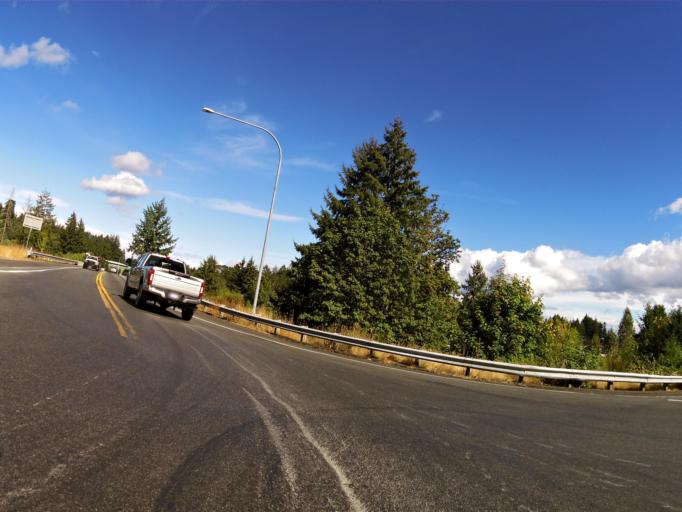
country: US
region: Washington
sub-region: Thurston County
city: Olympia
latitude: 47.0807
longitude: -123.0248
